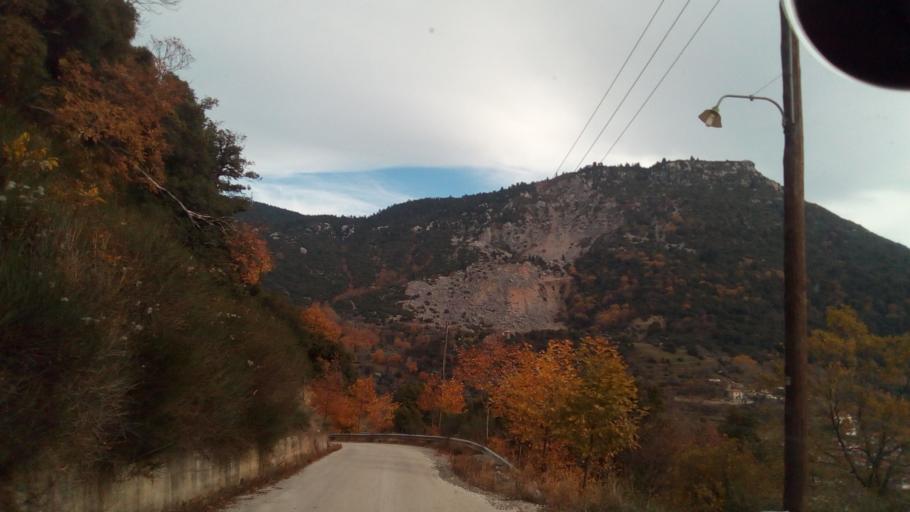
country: GR
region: West Greece
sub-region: Nomos Aitolias kai Akarnanias
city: Thermo
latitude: 38.6821
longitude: 21.9012
